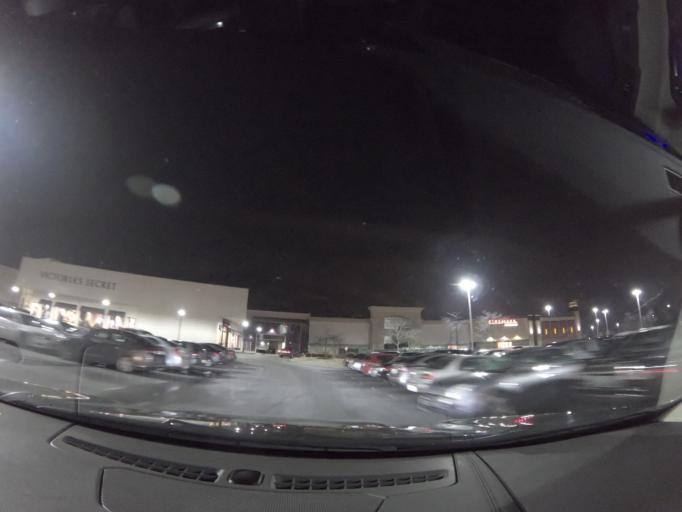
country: US
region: Kentucky
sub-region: Jefferson County
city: Beechwood Village
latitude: 38.2493
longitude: -85.6242
